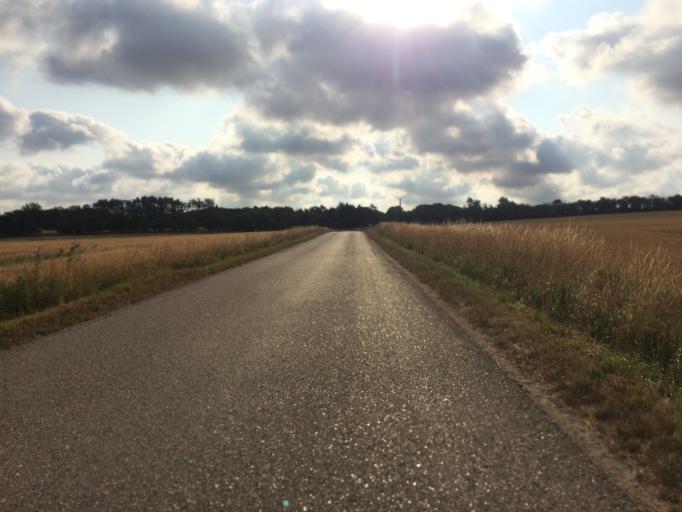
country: DK
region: Central Jutland
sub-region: Holstebro Kommune
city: Vinderup
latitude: 56.6072
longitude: 8.7982
